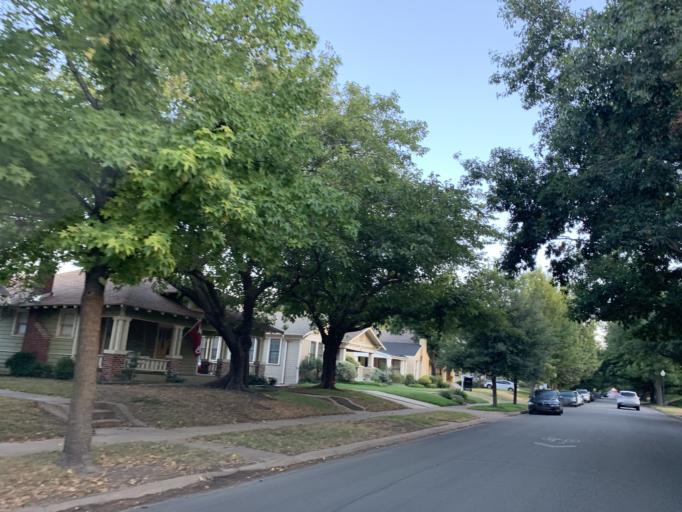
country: US
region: Texas
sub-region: Dallas County
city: Cockrell Hill
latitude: 32.7481
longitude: -96.8440
